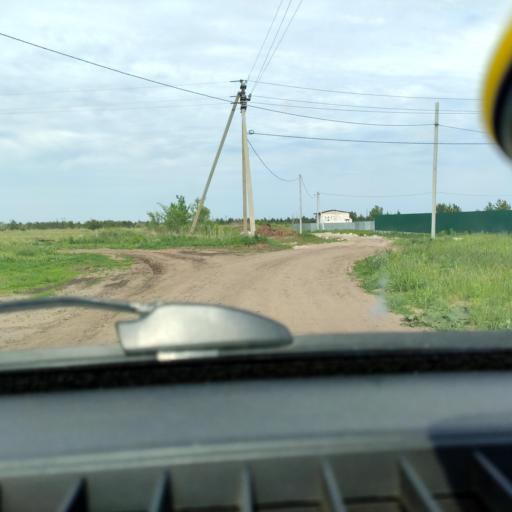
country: RU
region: Samara
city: Povolzhskiy
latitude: 53.5935
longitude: 49.5768
